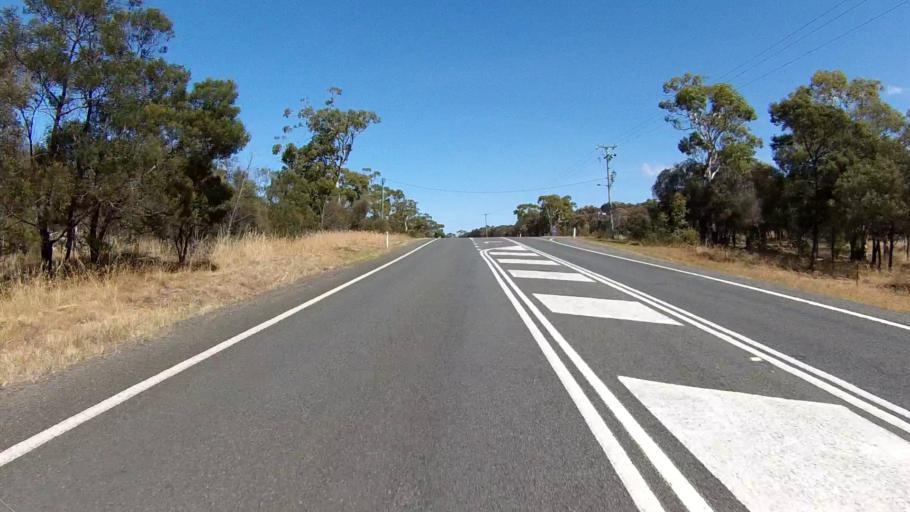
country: AU
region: Tasmania
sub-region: Sorell
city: Sorell
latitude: -42.1423
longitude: 148.0690
